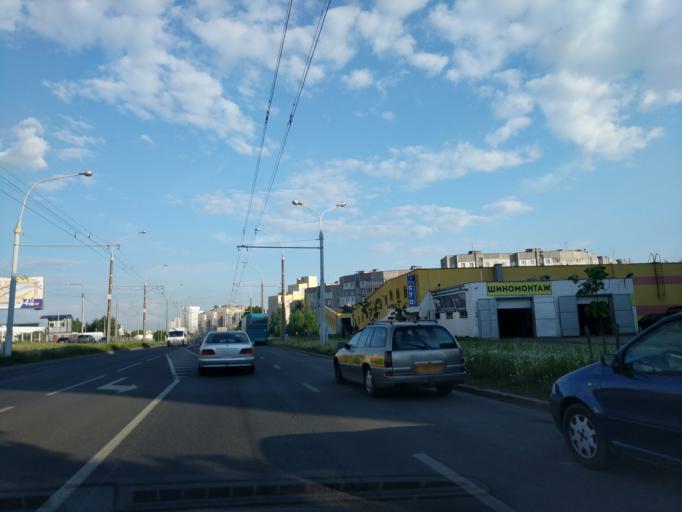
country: BY
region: Minsk
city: Novoye Medvezhino
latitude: 53.8876
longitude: 27.4439
